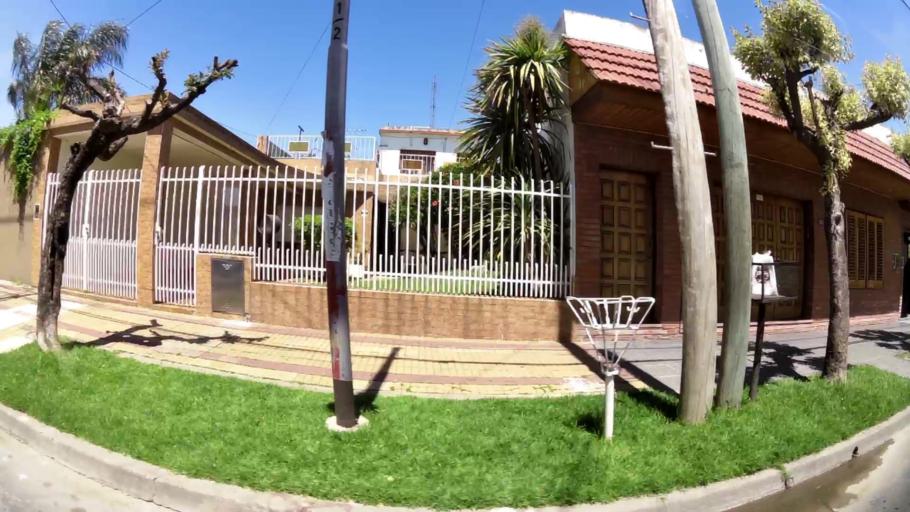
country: AR
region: Buenos Aires
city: Caseros
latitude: -34.5844
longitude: -58.5689
